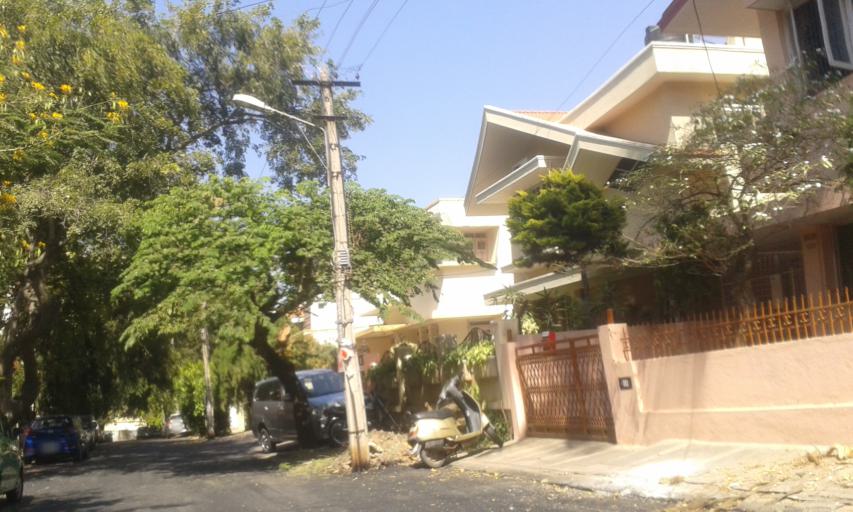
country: IN
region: Karnataka
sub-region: Bangalore Urban
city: Bangalore
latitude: 12.9248
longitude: 77.5890
